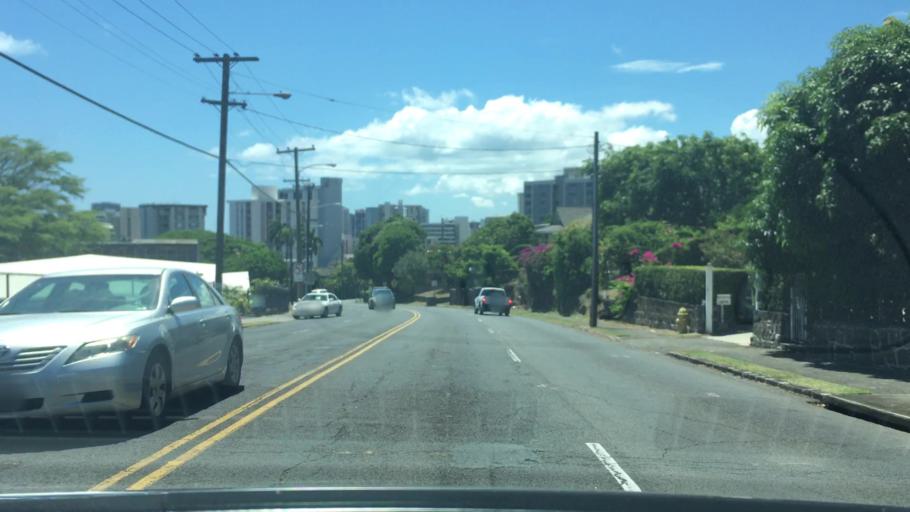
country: US
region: Hawaii
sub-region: Honolulu County
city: Honolulu
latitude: 21.3053
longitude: -157.8284
